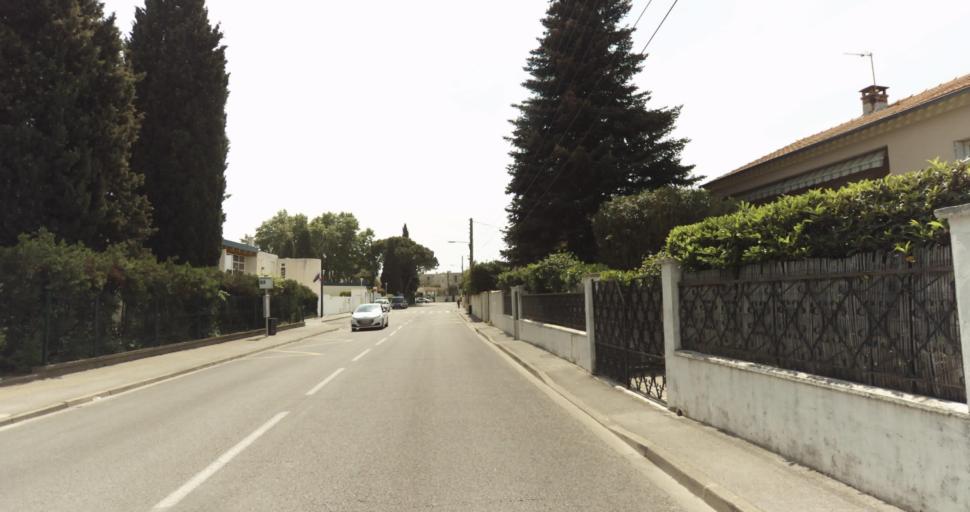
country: FR
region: Languedoc-Roussillon
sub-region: Departement du Gard
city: Nimes
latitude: 43.8353
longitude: 4.3841
